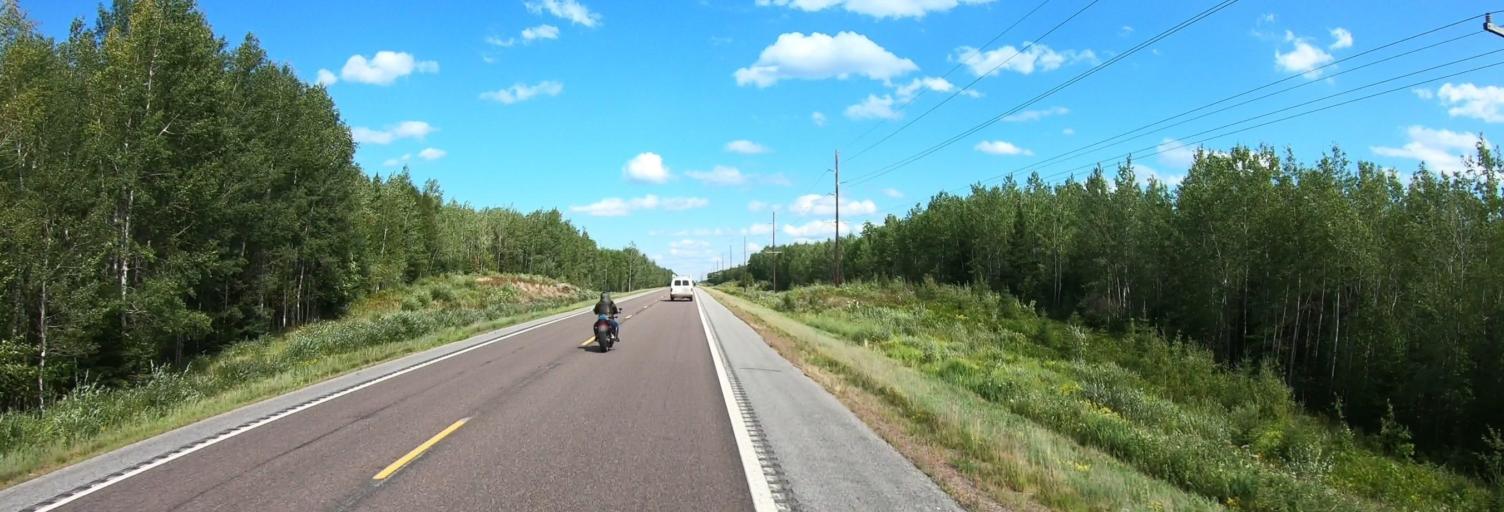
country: US
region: Minnesota
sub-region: Saint Louis County
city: Virginia
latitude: 47.8587
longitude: -92.4575
